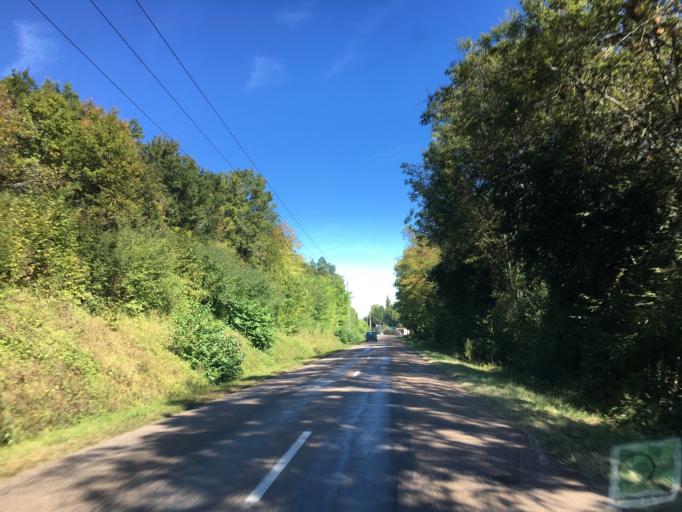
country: FR
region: Bourgogne
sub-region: Departement de l'Yonne
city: Vermenton
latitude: 47.6383
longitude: 3.6573
